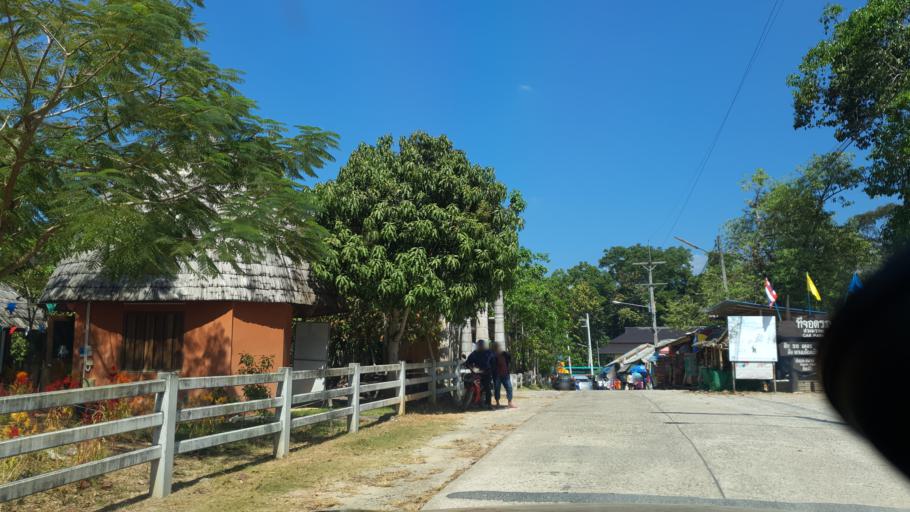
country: TH
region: Krabi
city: Khlong Thom
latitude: 7.9218
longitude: 99.2598
